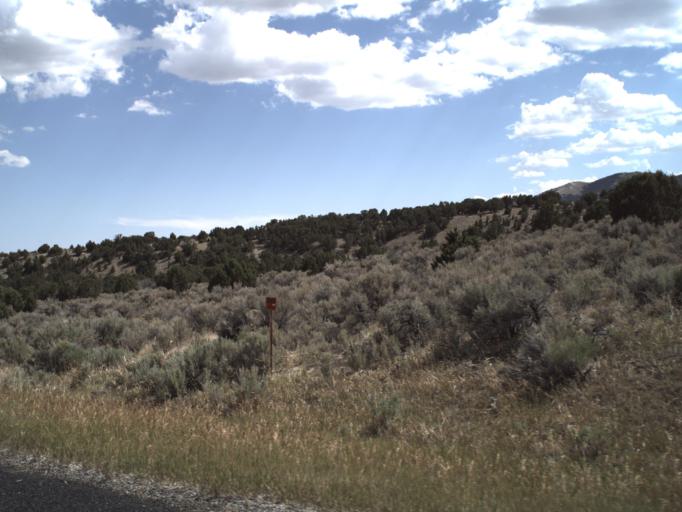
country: US
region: Idaho
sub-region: Minidoka County
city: Rupert
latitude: 41.9825
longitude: -113.1706
